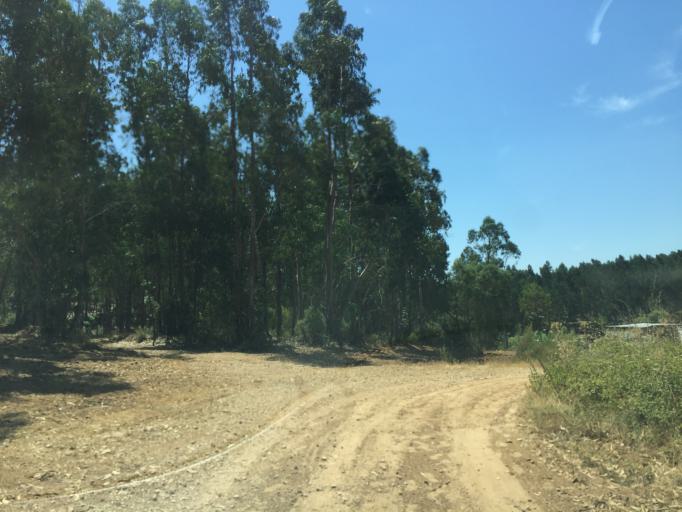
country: PT
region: Santarem
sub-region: Tomar
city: Tomar
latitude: 39.6026
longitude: -8.3580
